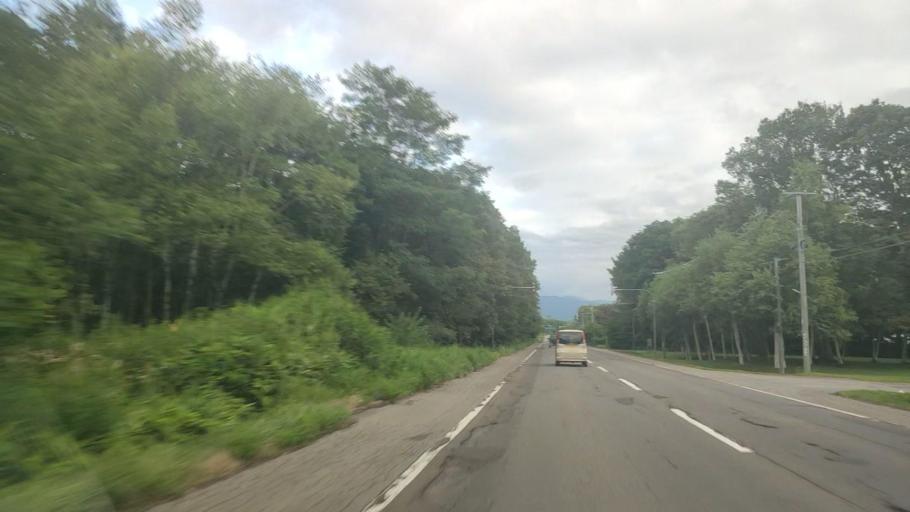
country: JP
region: Hokkaido
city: Nanae
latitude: 42.0136
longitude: 140.6255
